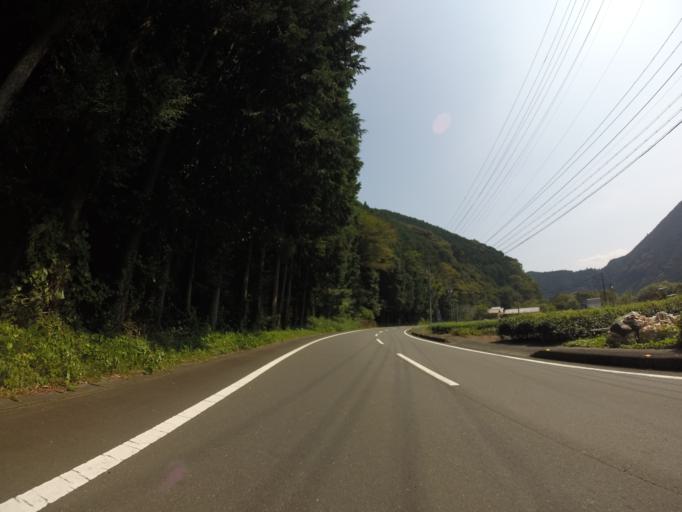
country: JP
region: Shizuoka
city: Shizuoka-shi
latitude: 35.1424
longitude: 138.3660
